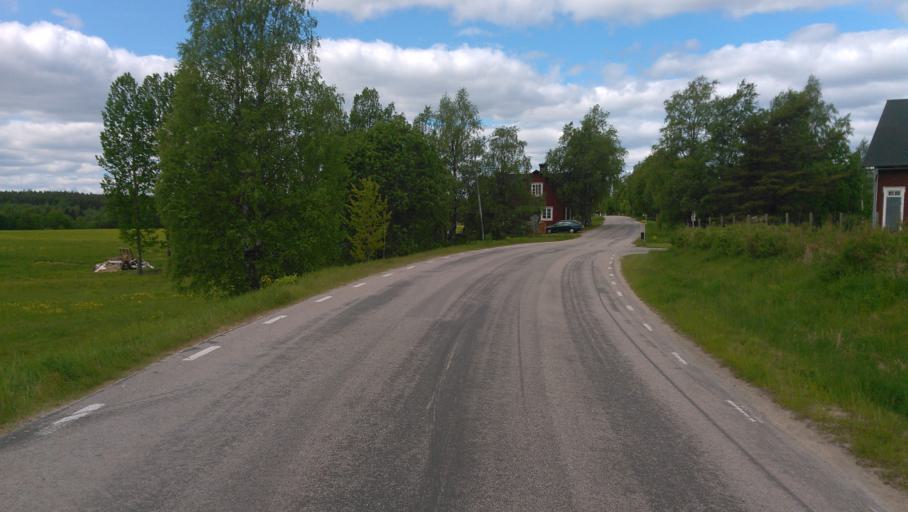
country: SE
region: Vaesterbotten
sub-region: Umea Kommun
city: Roback
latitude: 63.8637
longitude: 20.0848
